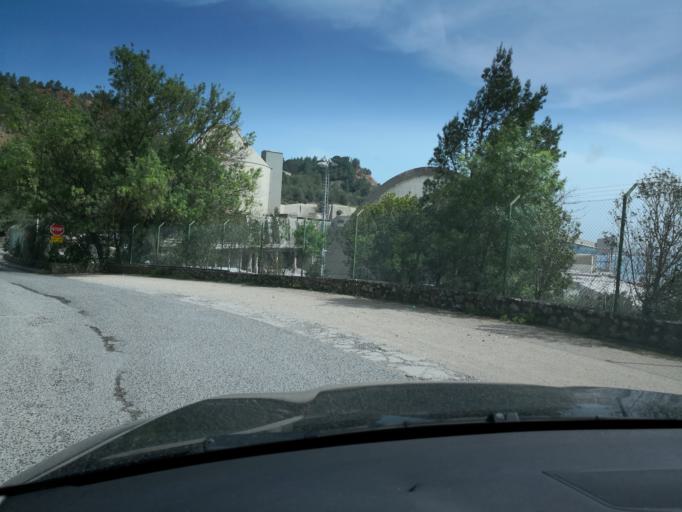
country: PT
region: Setubal
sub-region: Setubal
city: Setubal
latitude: 38.4912
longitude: -8.9342
